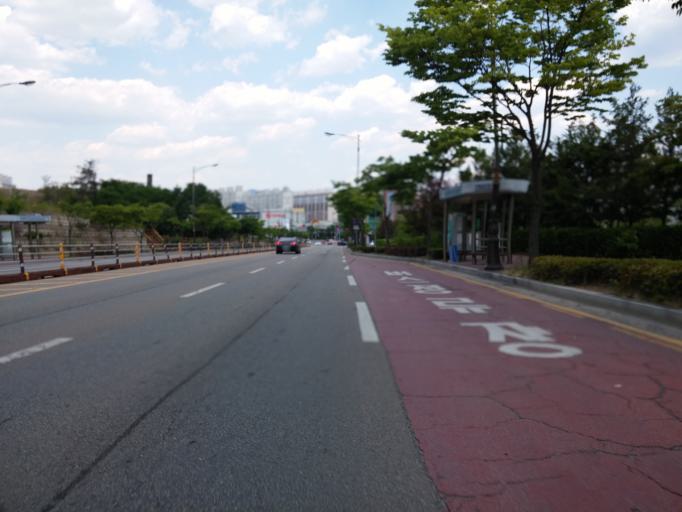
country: KR
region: Chungcheongbuk-do
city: Cheongju-si
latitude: 36.6152
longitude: 127.4668
